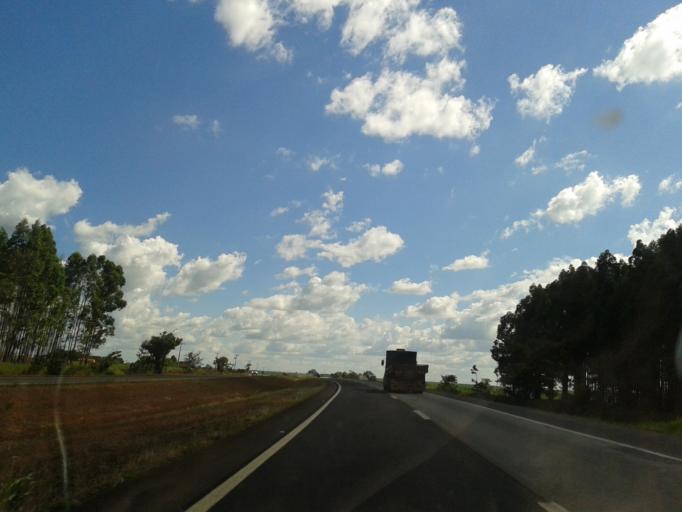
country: BR
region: Goias
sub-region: Morrinhos
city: Morrinhos
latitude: -17.8013
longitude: -49.2065
